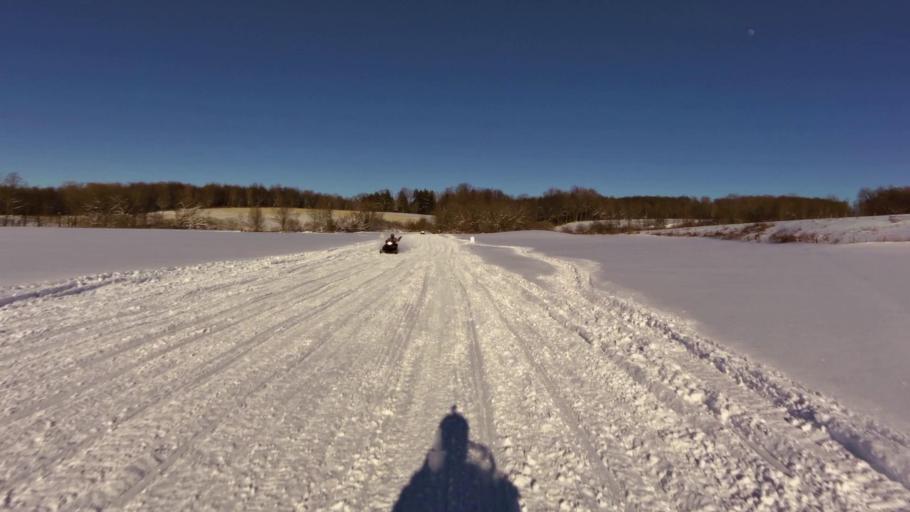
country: US
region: New York
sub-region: Chautauqua County
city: Mayville
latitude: 42.2756
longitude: -79.4698
